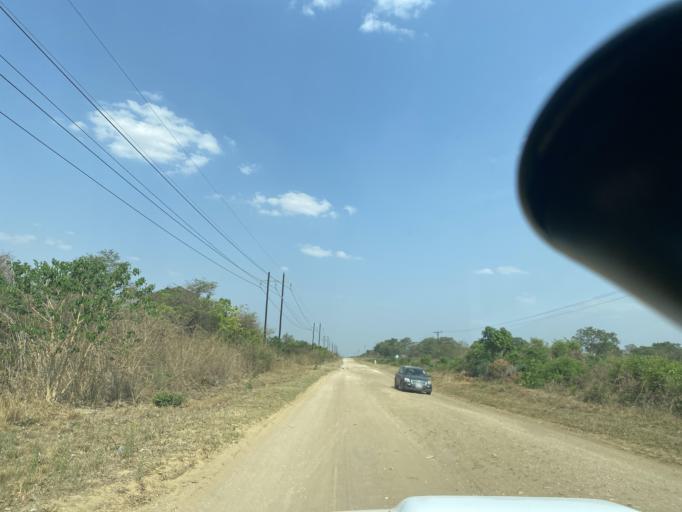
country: ZM
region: Lusaka
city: Lusaka
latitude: -15.3085
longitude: 28.0441
